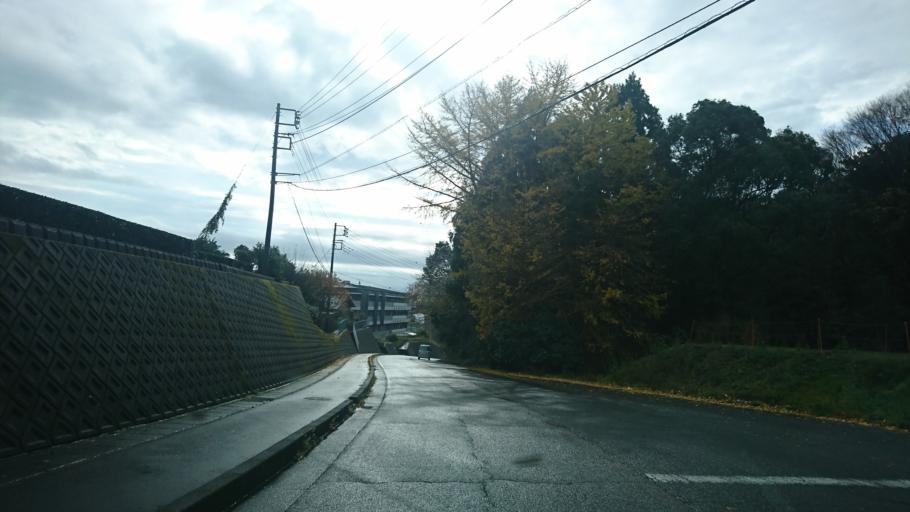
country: JP
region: Shizuoka
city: Fuji
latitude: 35.1885
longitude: 138.7235
